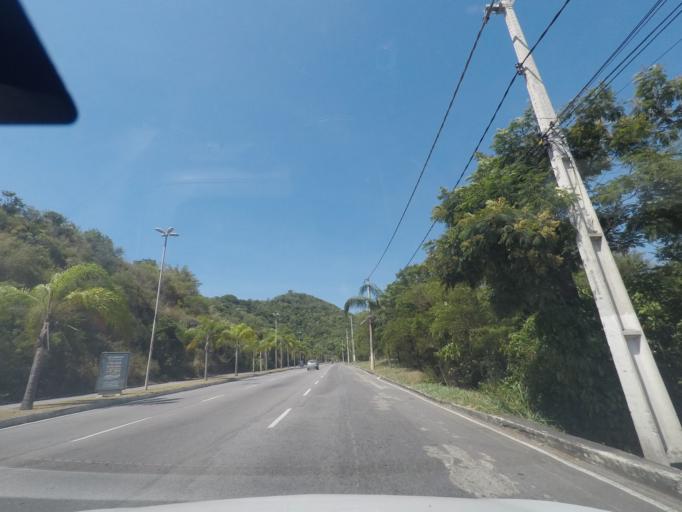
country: BR
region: Rio de Janeiro
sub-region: Niteroi
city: Niteroi
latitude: -22.9262
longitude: -43.0617
